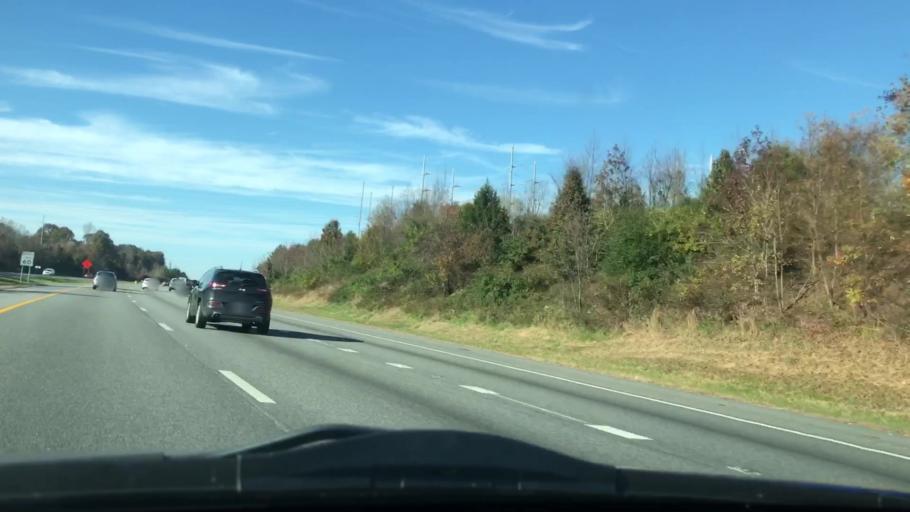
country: US
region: North Carolina
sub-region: Guilford County
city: High Point
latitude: 35.9926
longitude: -79.9845
